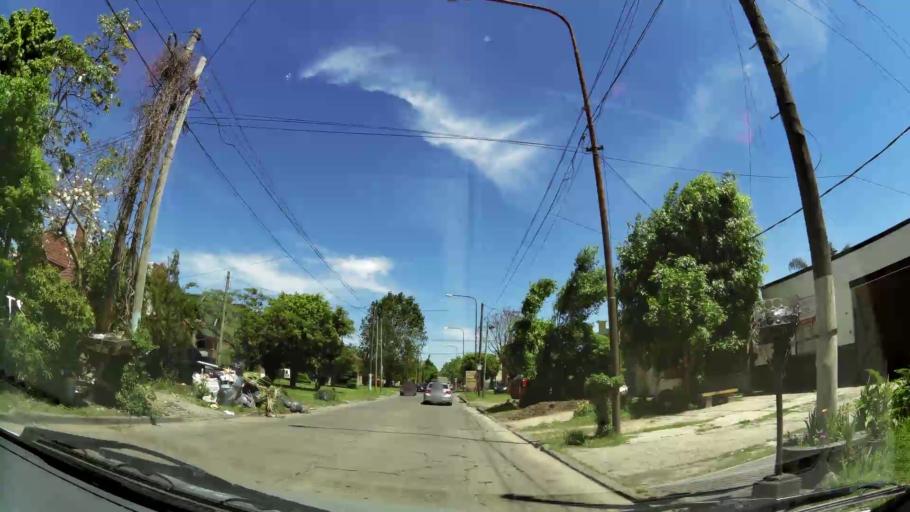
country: AR
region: Buenos Aires
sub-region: Partido de Quilmes
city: Quilmes
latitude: -34.7344
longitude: -58.2827
